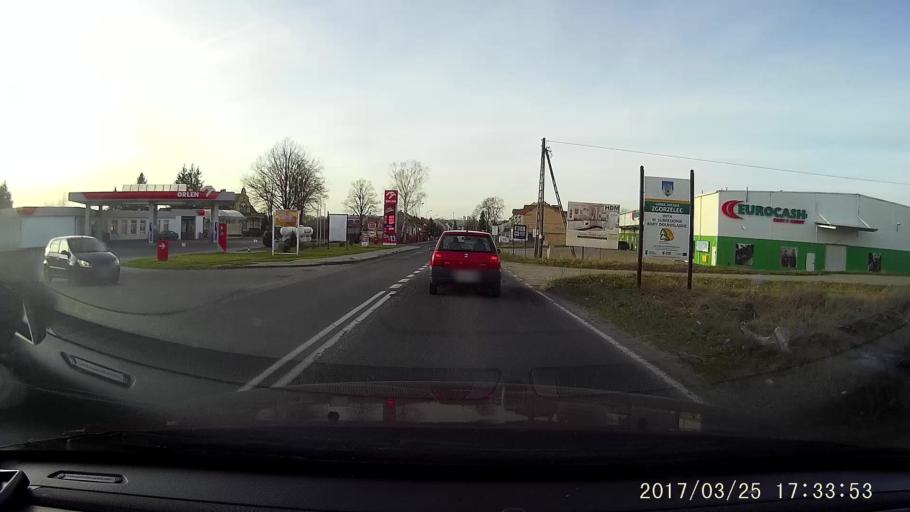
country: PL
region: Lower Silesian Voivodeship
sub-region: Powiat zgorzelecki
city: Zgorzelec
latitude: 51.1271
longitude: 15.0162
